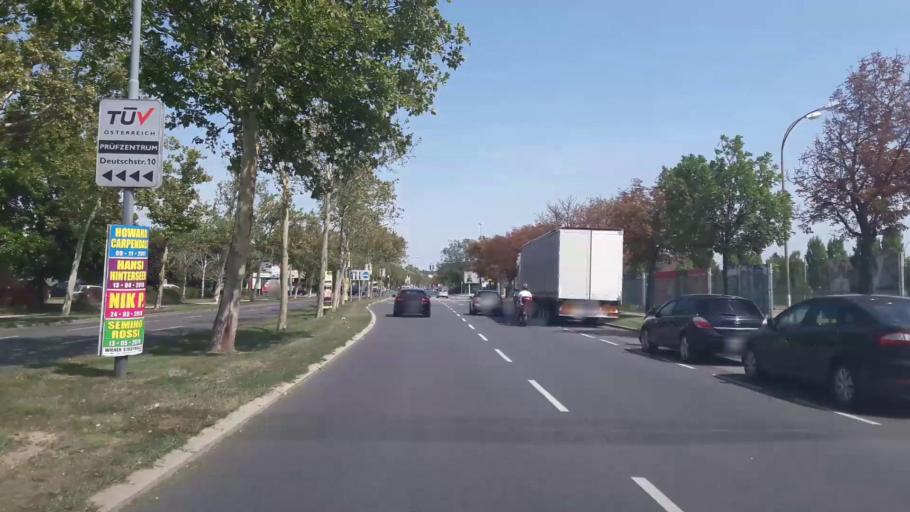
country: AT
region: Lower Austria
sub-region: Politischer Bezirk Modling
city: Vosendorf
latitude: 48.1384
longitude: 16.3582
